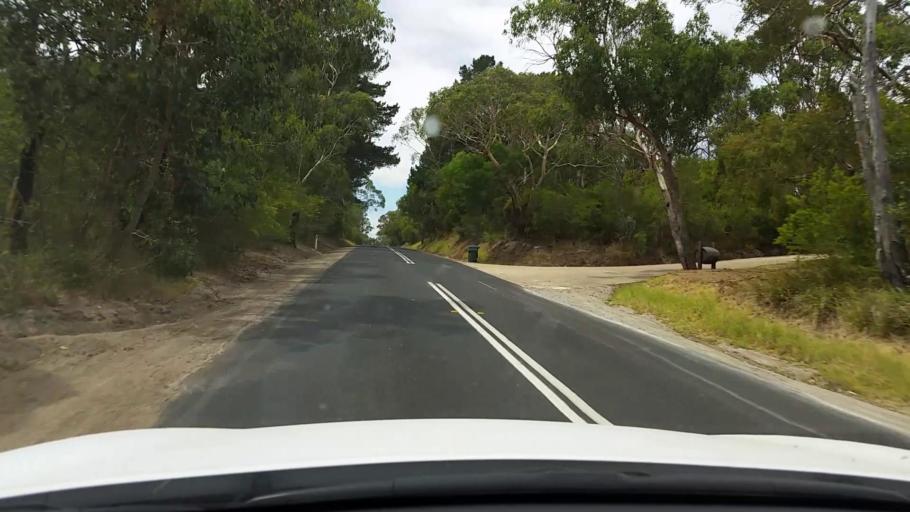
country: AU
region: Victoria
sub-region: Mornington Peninsula
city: Mount Martha
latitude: -38.2880
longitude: 145.0599
